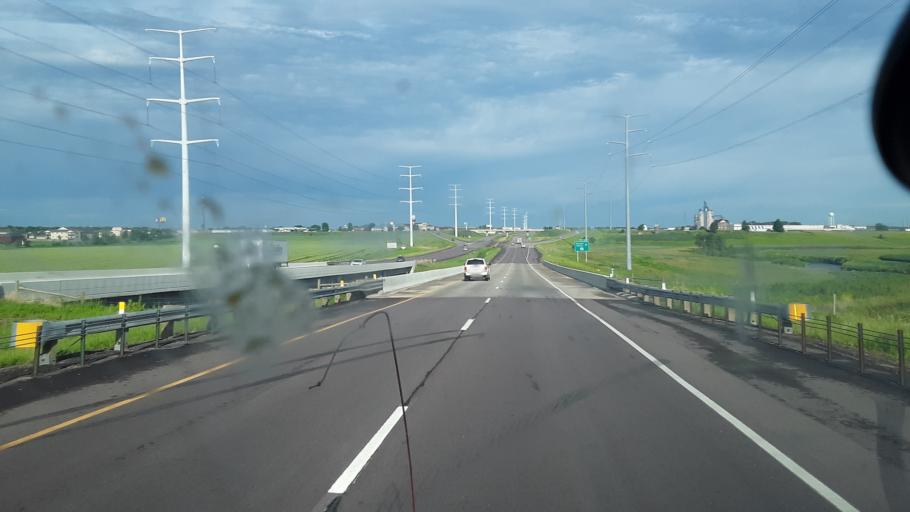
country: US
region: South Dakota
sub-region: Minnehaha County
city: Brandon
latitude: 43.6086
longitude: -96.5624
